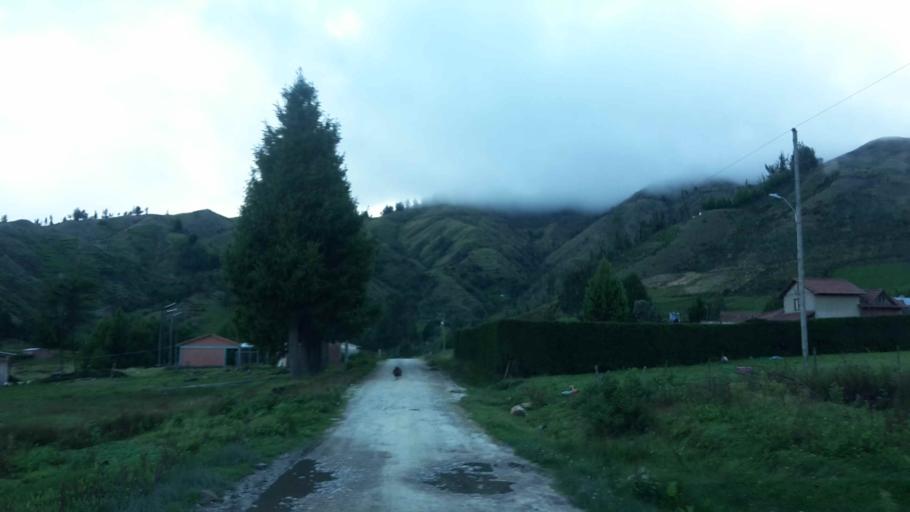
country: BO
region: Cochabamba
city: Colomi
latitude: -17.2454
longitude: -65.9053
